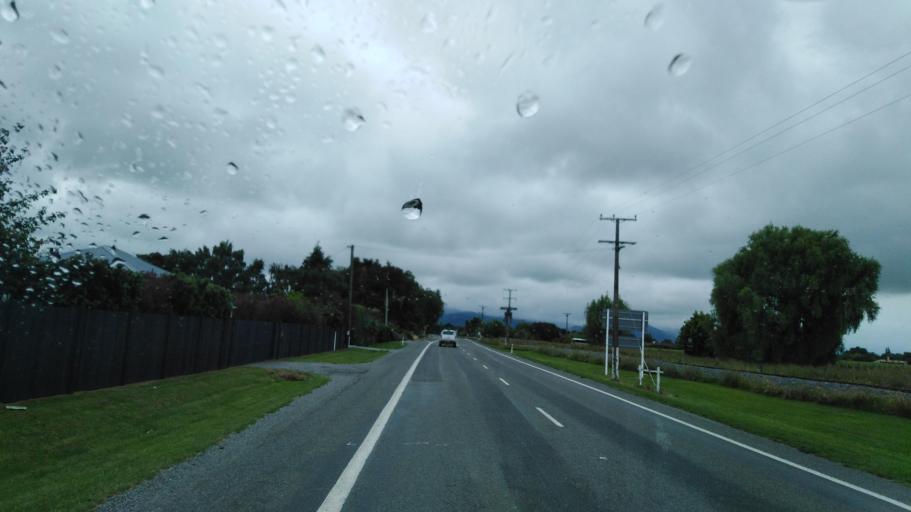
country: NZ
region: Marlborough
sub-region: Marlborough District
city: Blenheim
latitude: -41.4893
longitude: 173.9649
